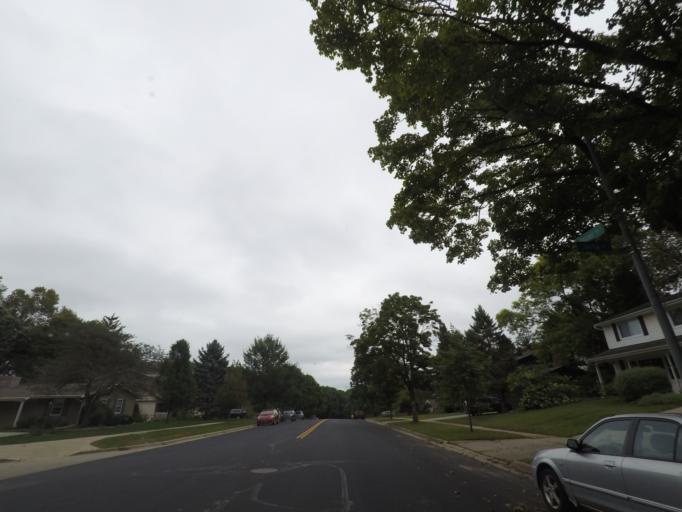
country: US
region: Wisconsin
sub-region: Dane County
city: Middleton
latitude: 43.0675
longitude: -89.4896
